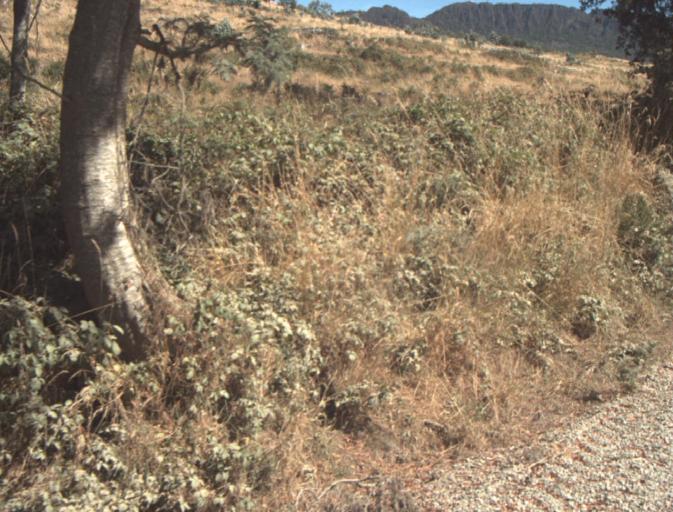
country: AU
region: Tasmania
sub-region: Dorset
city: Scottsdale
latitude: -41.3465
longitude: 147.4438
